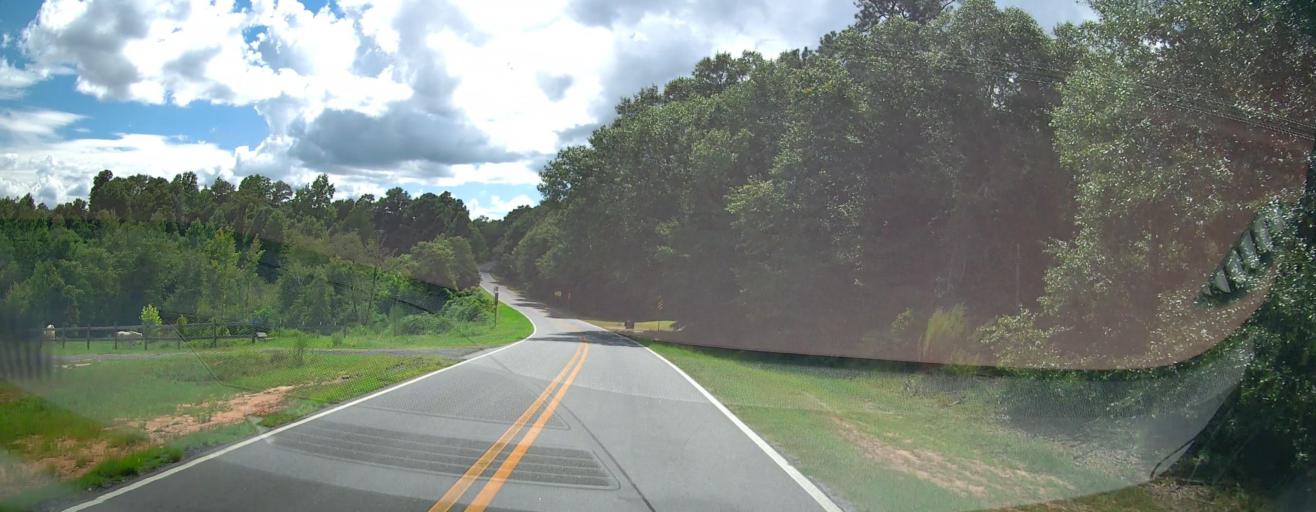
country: US
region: Georgia
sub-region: Chattahoochee County
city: Cusseta
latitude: 32.3064
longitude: -84.7682
